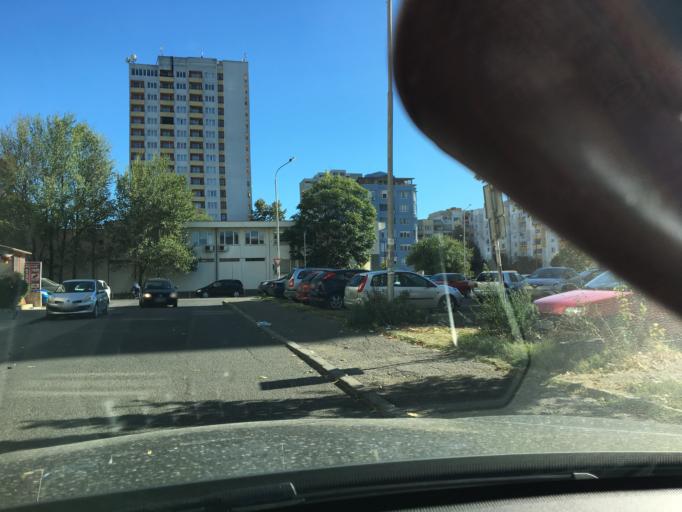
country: BG
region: Burgas
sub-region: Obshtina Burgas
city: Burgas
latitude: 42.5208
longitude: 27.4502
